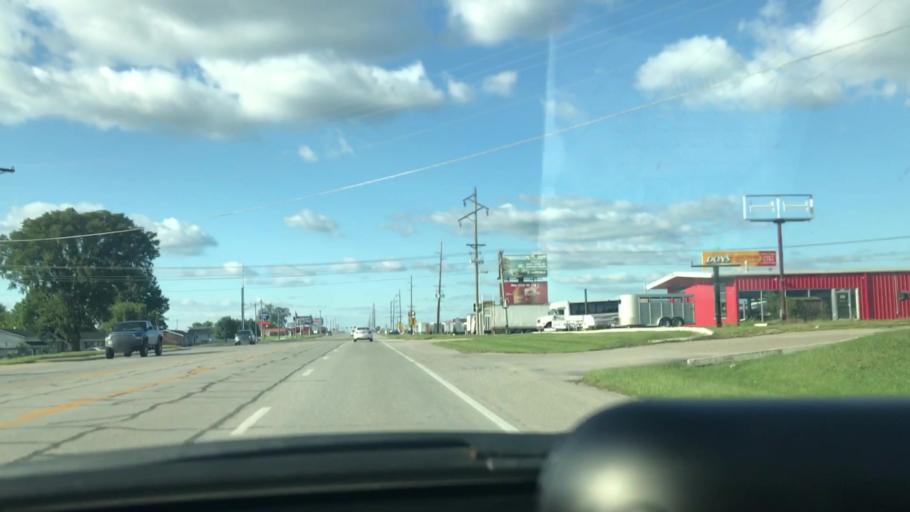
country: US
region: Missouri
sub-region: Pettis County
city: Sedalia
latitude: 38.6685
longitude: -93.2518
